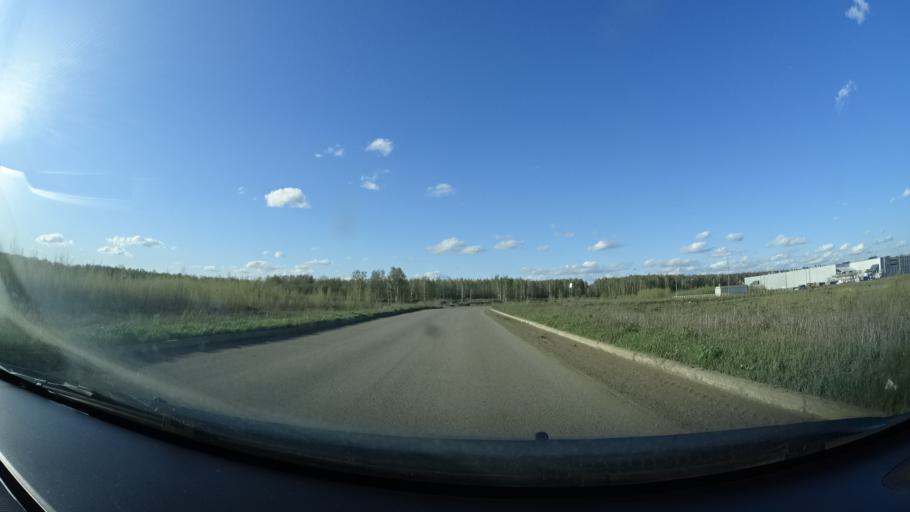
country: RU
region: Bashkortostan
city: Ufa
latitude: 54.6785
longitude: 55.9255
